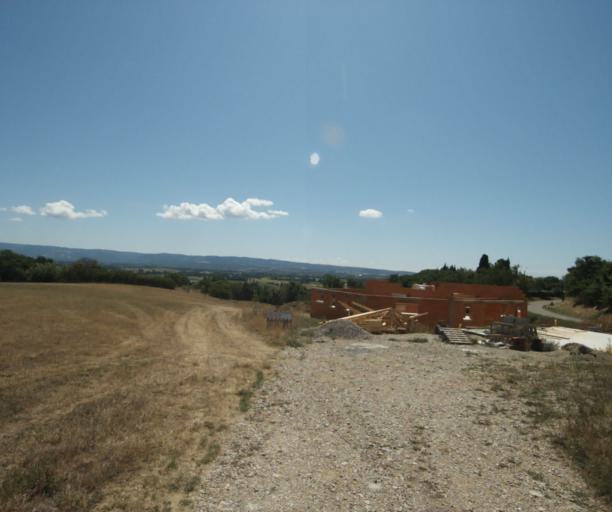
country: FR
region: Midi-Pyrenees
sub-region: Departement de la Haute-Garonne
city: Saint-Felix-Lauragais
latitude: 43.4951
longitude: 1.9290
